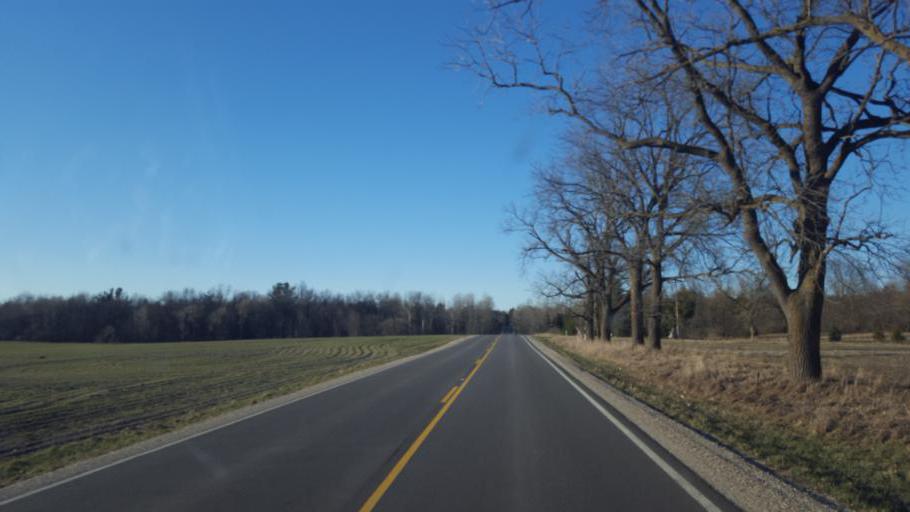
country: US
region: Michigan
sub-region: Mecosta County
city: Canadian Lakes
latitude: 43.5336
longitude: -85.2543
